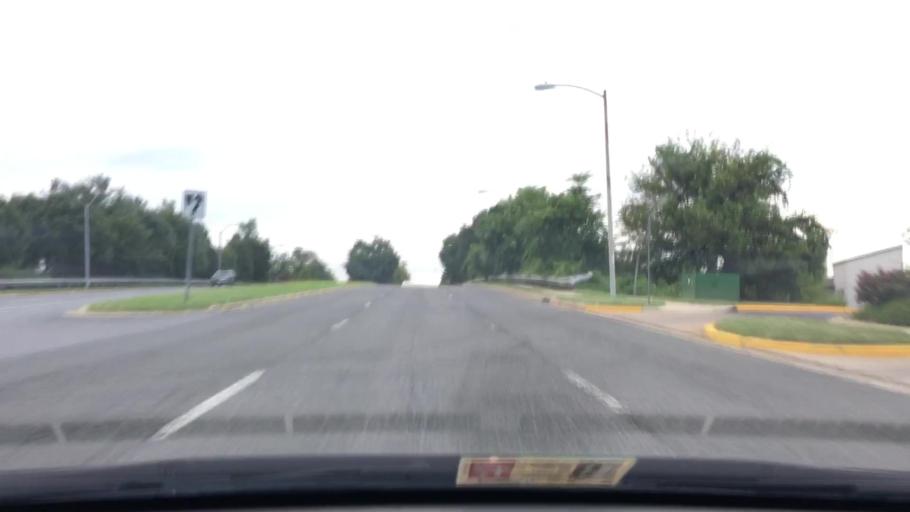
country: US
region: Maryland
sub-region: Prince George's County
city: Laurel
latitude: 39.0860
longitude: -76.8502
